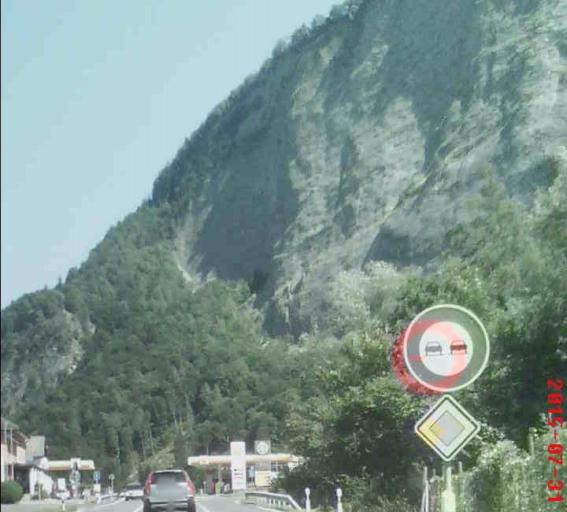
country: CH
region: Grisons
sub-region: Landquart District
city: Malans
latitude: 46.9701
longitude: 9.5936
